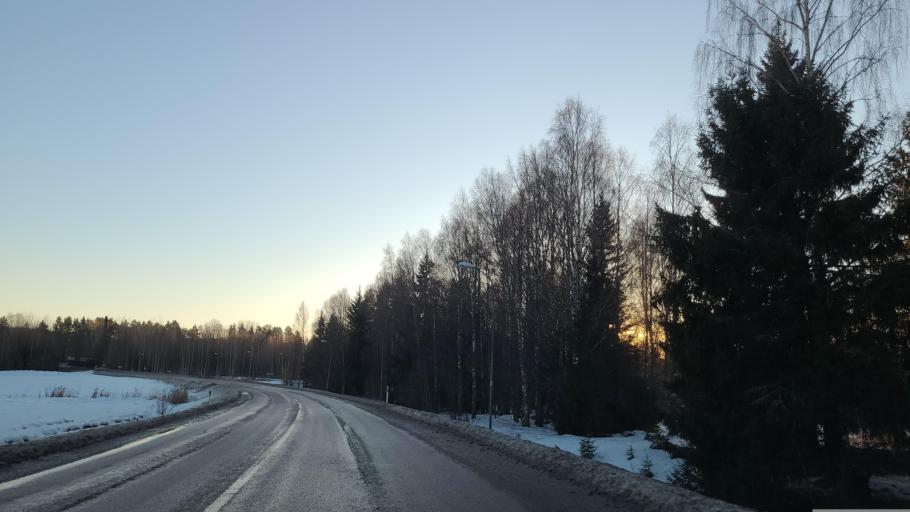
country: SE
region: Gaevleborg
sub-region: Soderhamns Kommun
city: Soderhamn
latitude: 61.2818
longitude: 16.9701
